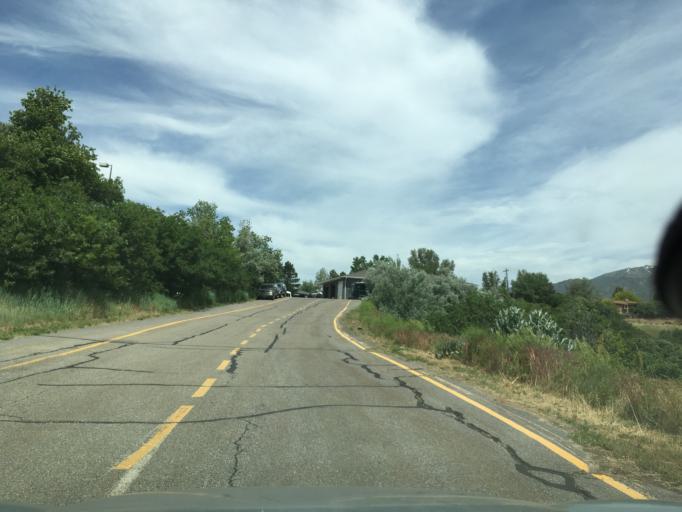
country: US
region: Utah
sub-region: Davis County
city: South Weber
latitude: 41.1047
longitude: -111.9209
